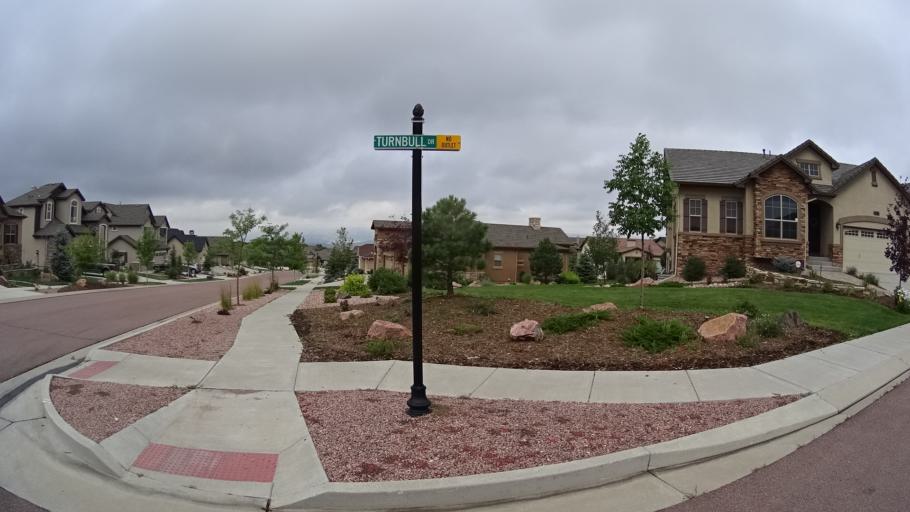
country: US
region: Colorado
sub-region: El Paso County
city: Gleneagle
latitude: 39.0285
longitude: -104.7911
